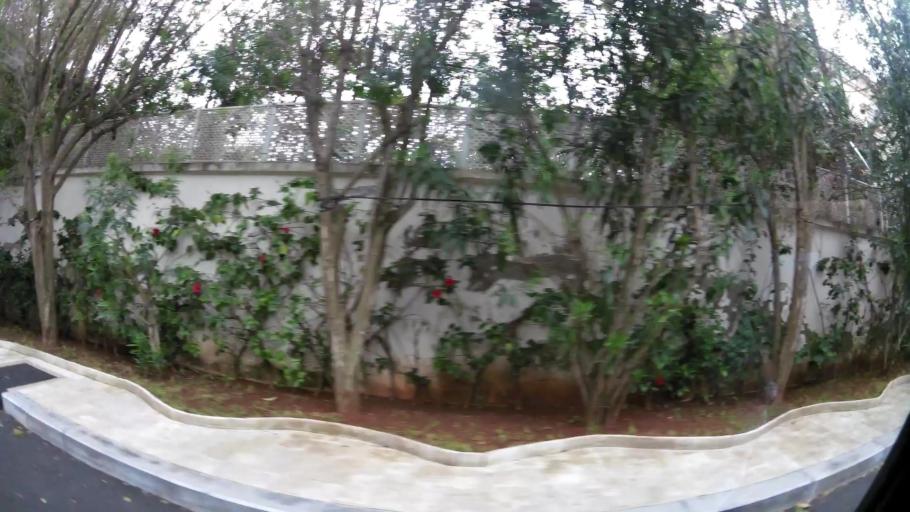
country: MA
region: Grand Casablanca
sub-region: Casablanca
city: Casablanca
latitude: 33.5845
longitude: -7.6633
